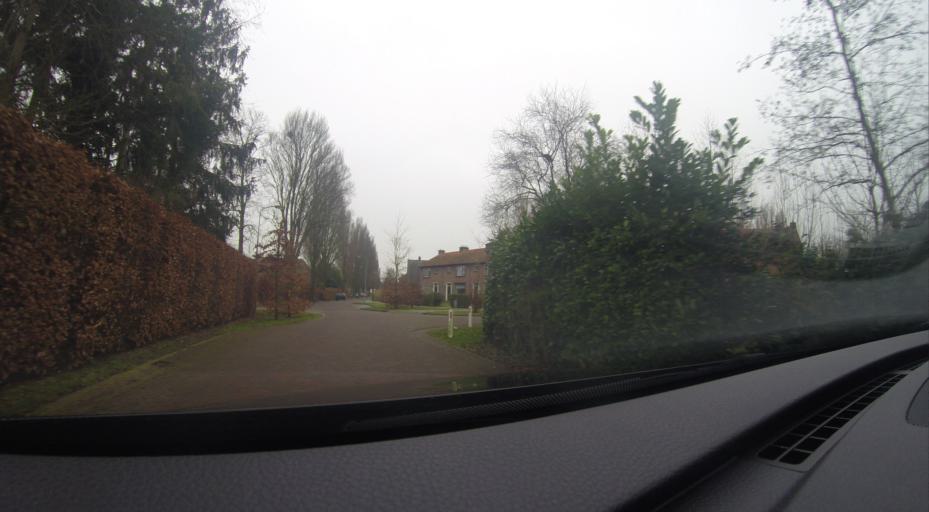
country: NL
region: Gelderland
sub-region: Gemeente Voorst
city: Voorst
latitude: 52.1692
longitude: 6.1465
